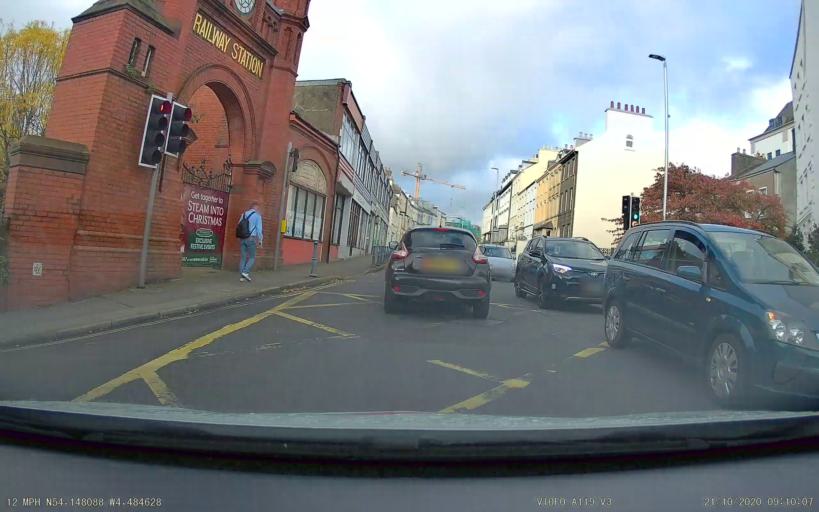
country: IM
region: Douglas
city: Douglas
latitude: 54.1481
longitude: -4.4847
